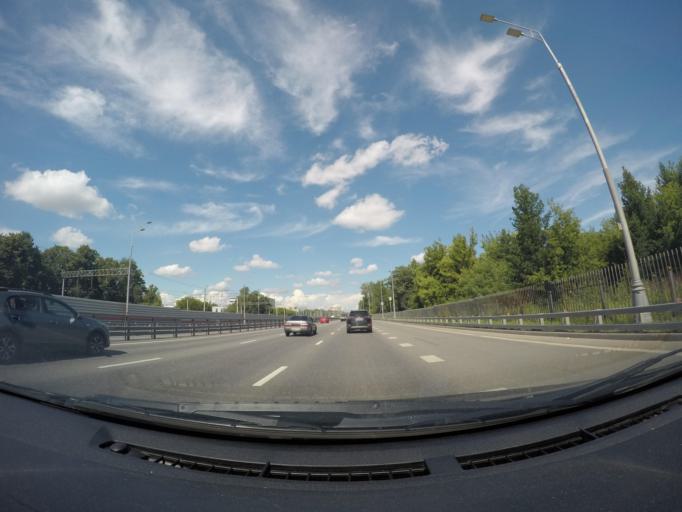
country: RU
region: Moscow
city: Perovo
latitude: 55.7257
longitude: 37.7906
